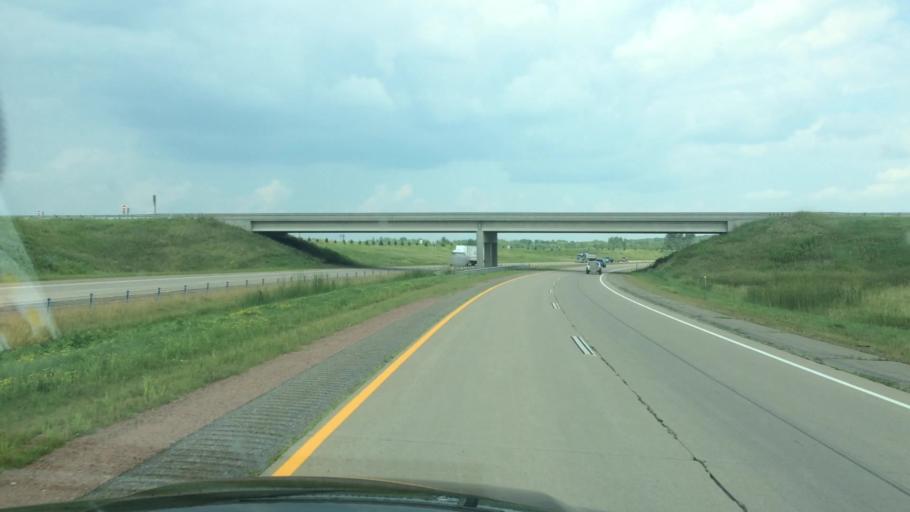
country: US
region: Wisconsin
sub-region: Clark County
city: Abbotsford
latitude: 44.9432
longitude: -90.2910
